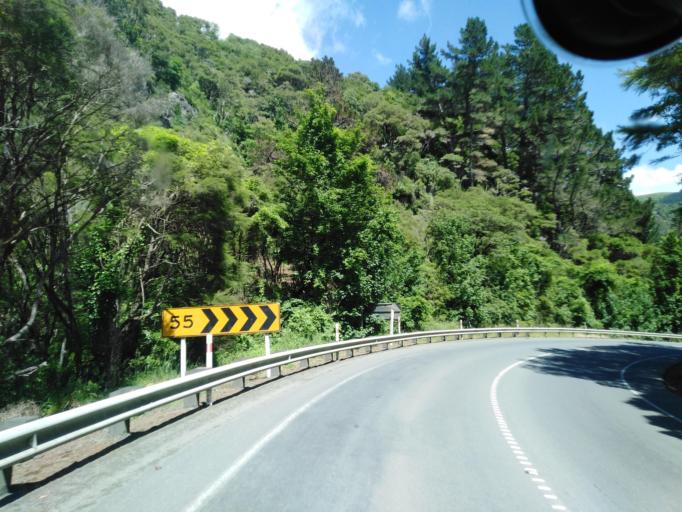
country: NZ
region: Nelson
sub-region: Nelson City
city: Nelson
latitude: -41.2299
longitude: 173.3999
